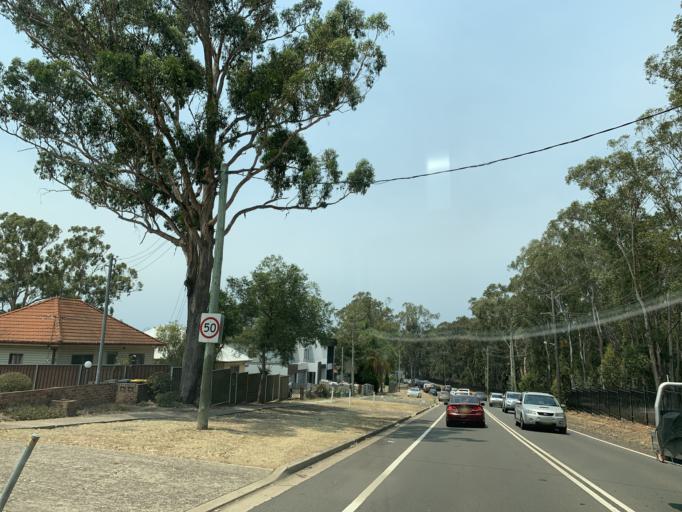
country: AU
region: New South Wales
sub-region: Blacktown
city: Blacktown
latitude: -33.7806
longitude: 150.9281
